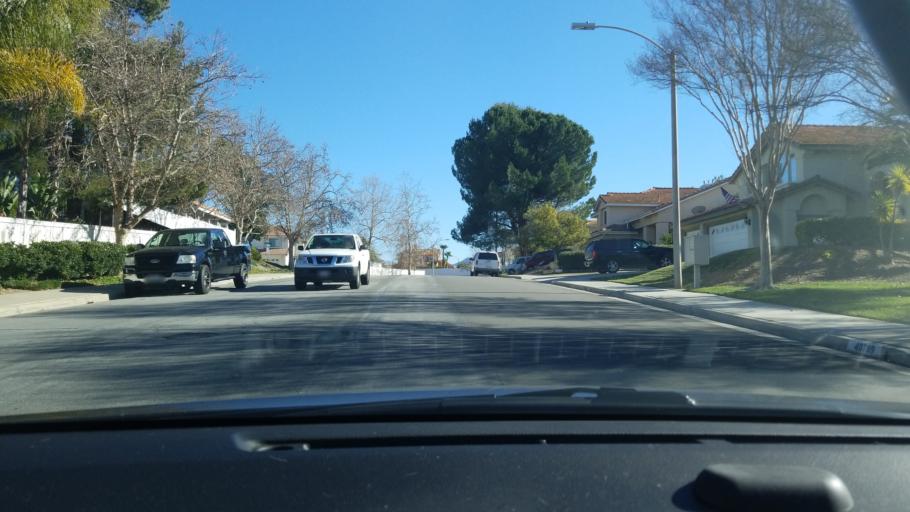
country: US
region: California
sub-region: Riverside County
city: Temecula
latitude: 33.5290
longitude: -117.1078
